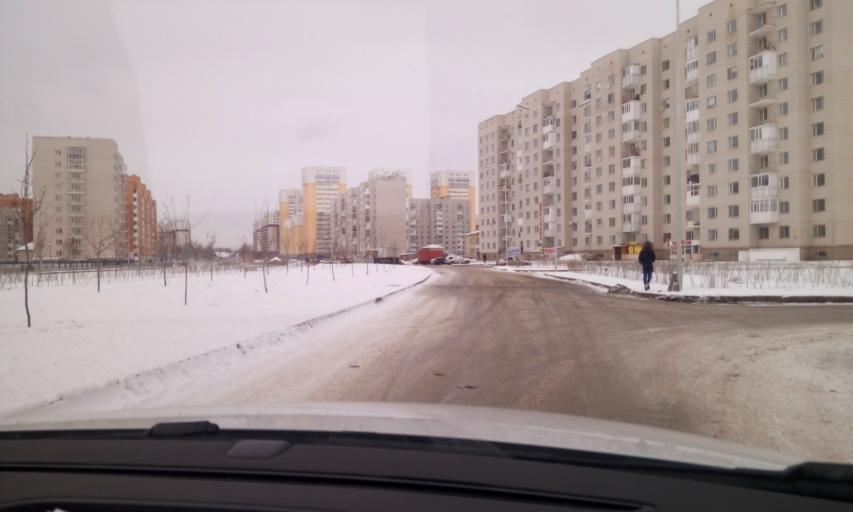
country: KZ
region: Astana Qalasy
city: Astana
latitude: 51.1247
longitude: 71.5052
